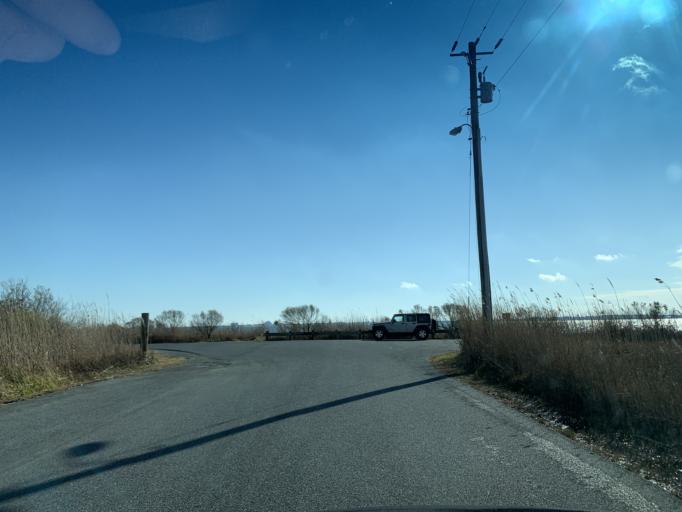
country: US
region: Maryland
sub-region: Worcester County
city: Ocean Pines
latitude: 38.3892
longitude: -75.1086
